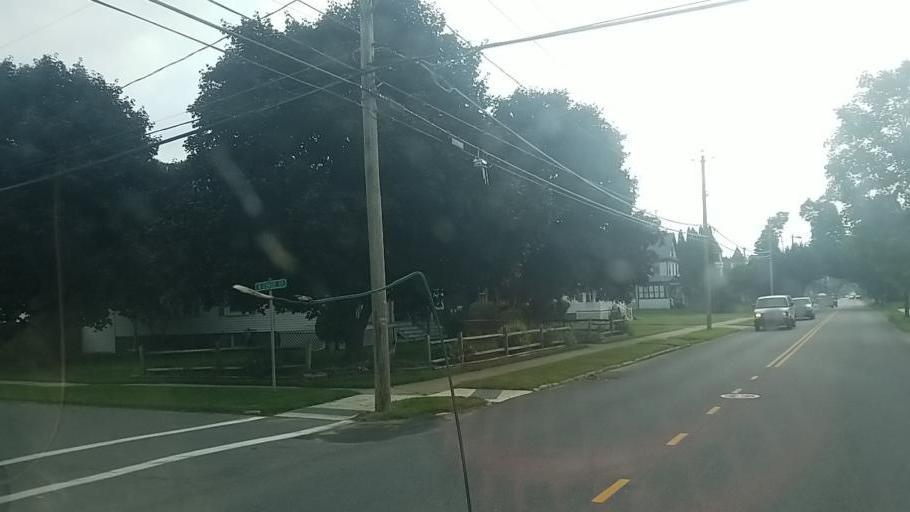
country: US
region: New York
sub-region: Fulton County
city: Johnstown
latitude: 43.0070
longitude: -74.3639
